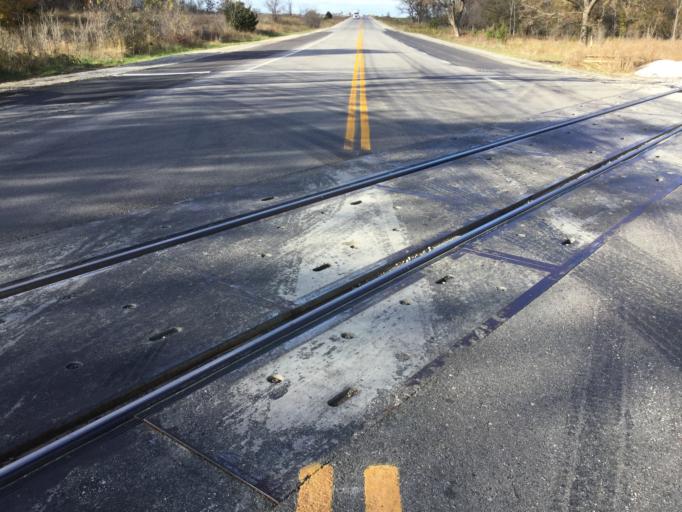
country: US
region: Kansas
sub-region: Montgomery County
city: Cherryvale
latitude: 37.1841
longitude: -95.5786
